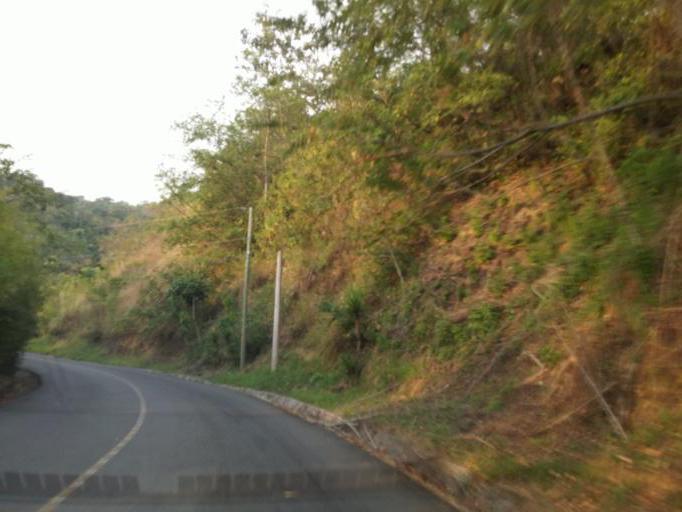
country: CR
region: San Jose
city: Palmichal
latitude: 9.8302
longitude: -84.2023
